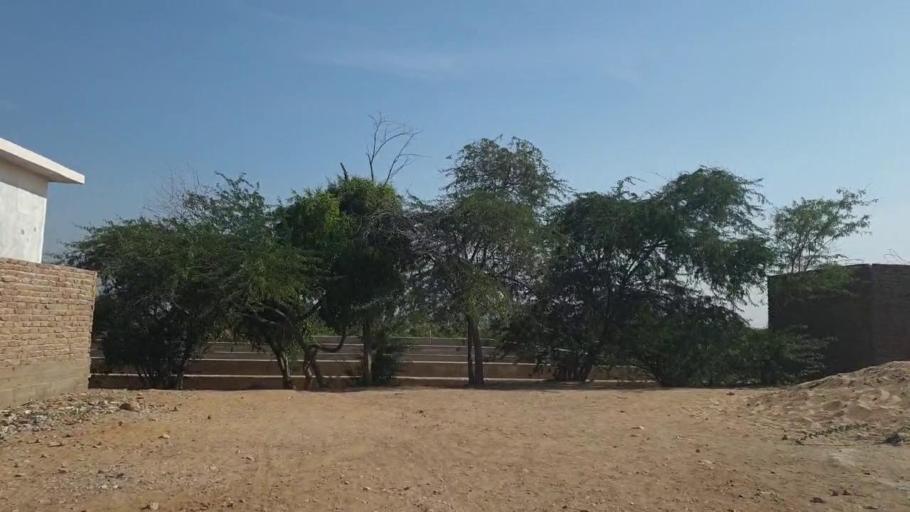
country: PK
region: Sindh
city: Matiari
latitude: 25.6805
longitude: 68.3020
